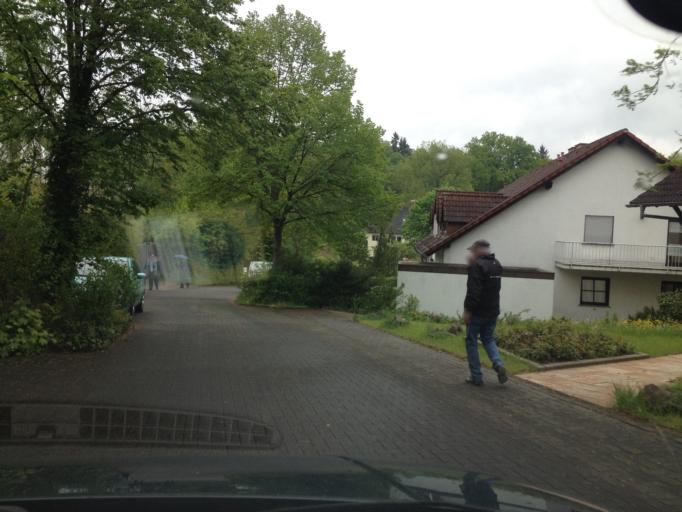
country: DE
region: Saarland
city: Sankt Wendel
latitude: 49.4649
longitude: 7.1814
